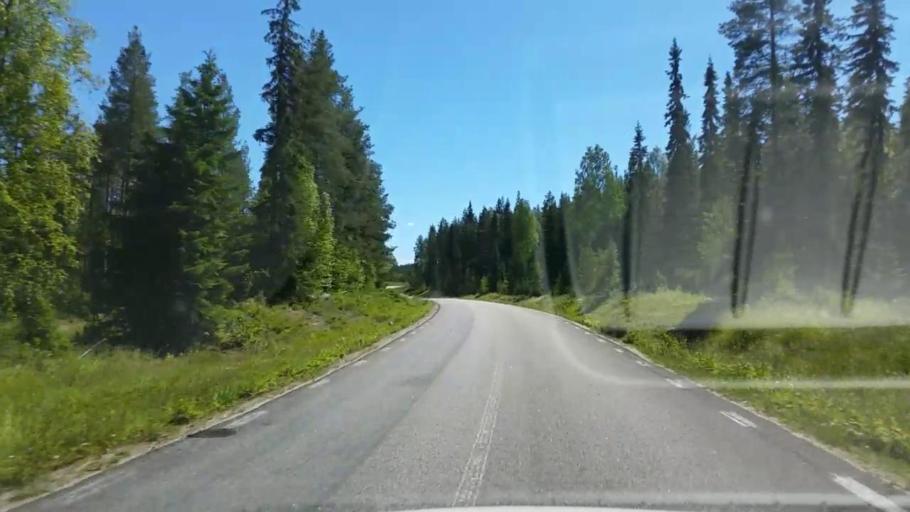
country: SE
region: Gaevleborg
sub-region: Ljusdals Kommun
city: Farila
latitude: 61.6491
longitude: 15.5896
